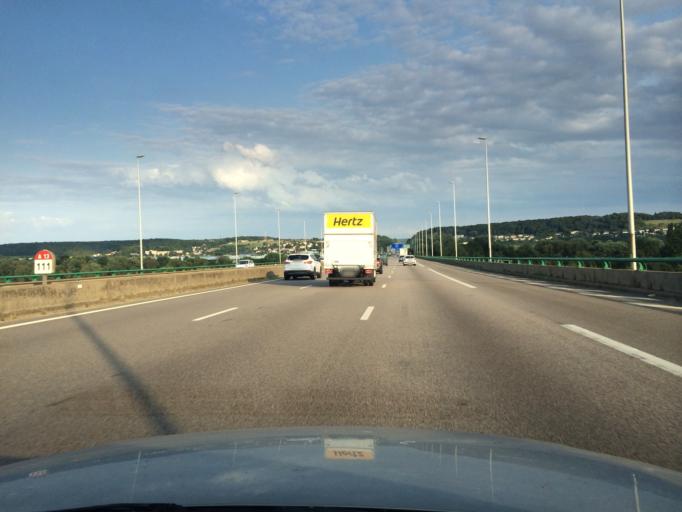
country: FR
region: Haute-Normandie
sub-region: Departement de la Seine-Maritime
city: Oissel
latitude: 49.3343
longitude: 1.0786
